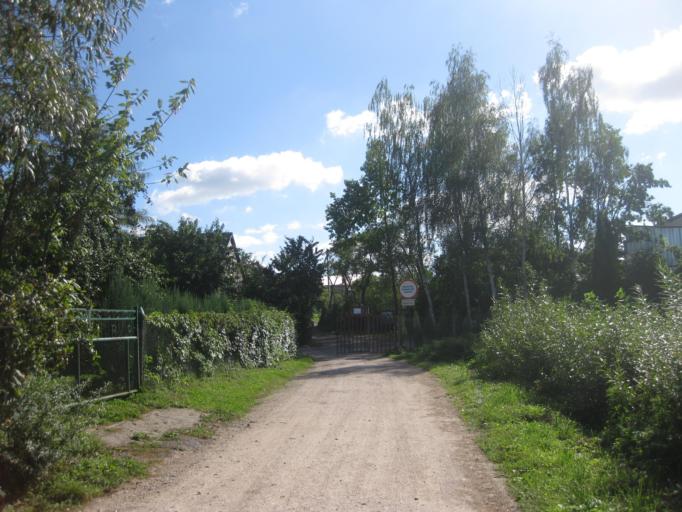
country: LT
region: Kauno apskritis
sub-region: Kauno rajonas
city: Garliava
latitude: 54.8290
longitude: 23.8826
